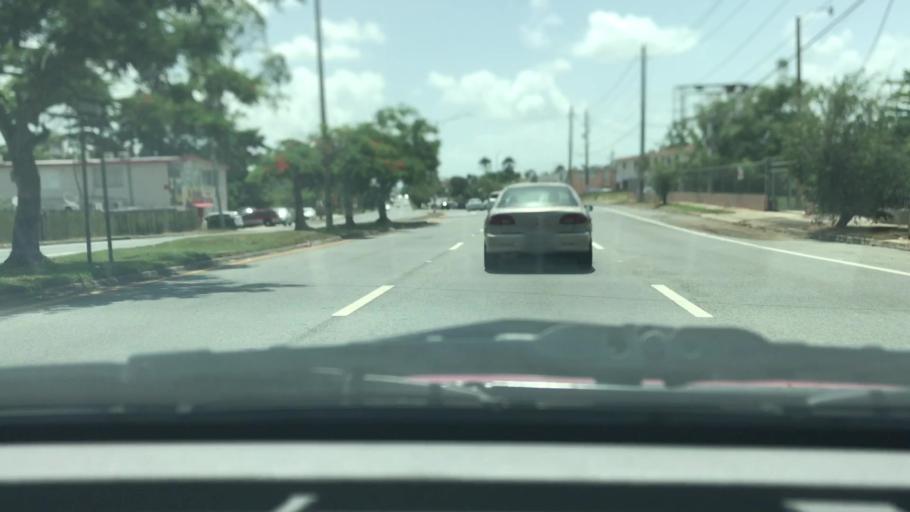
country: PR
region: Toa Alta
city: Pajaros
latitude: 18.3644
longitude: -66.1814
